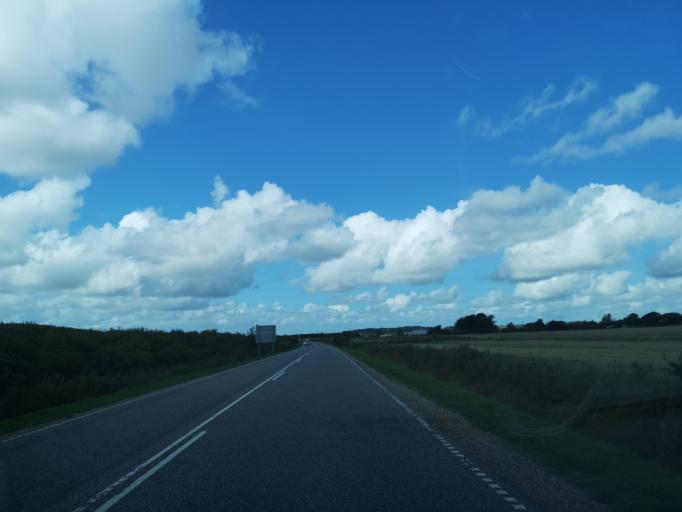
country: DK
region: Central Jutland
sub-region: Holstebro Kommune
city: Holstebro
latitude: 56.3897
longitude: 8.5966
